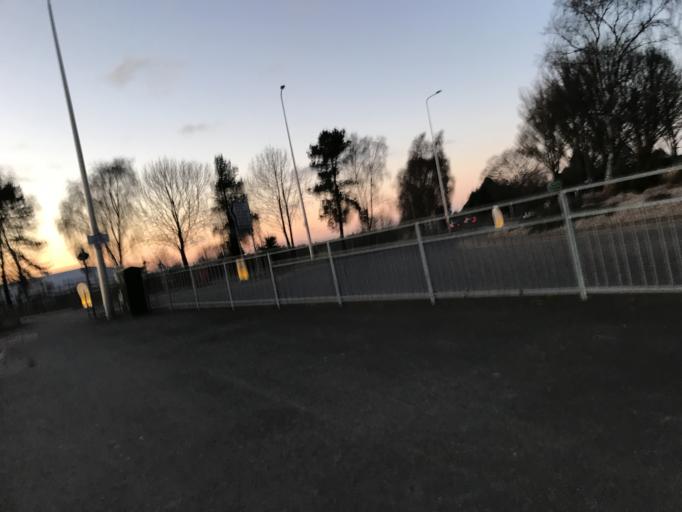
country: GB
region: England
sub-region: Lincolnshire
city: Holton le Clay
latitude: 53.5213
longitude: -0.0752
